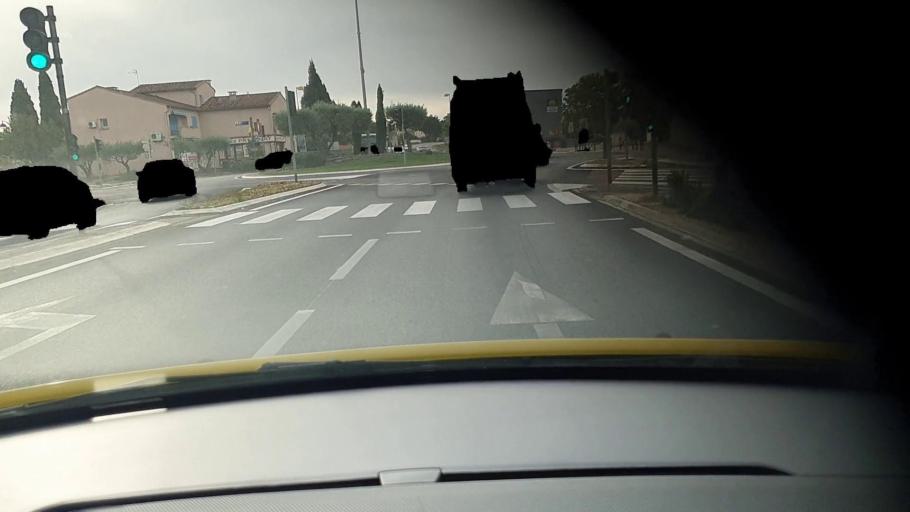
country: FR
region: Languedoc-Roussillon
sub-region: Departement du Gard
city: Caissargues
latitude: 43.7902
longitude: 4.3869
